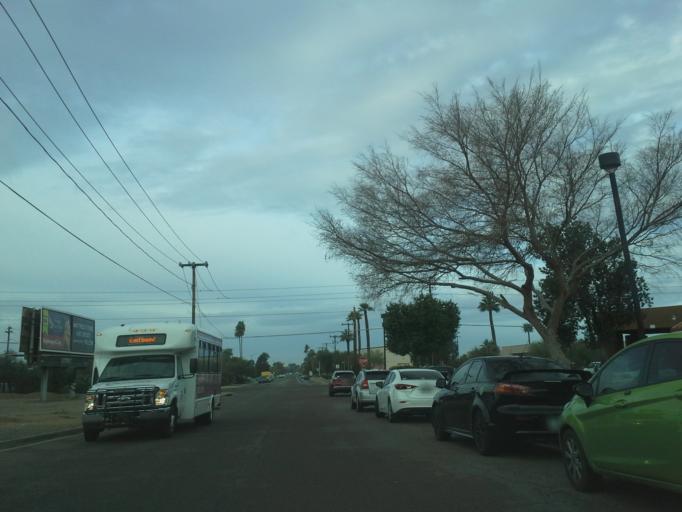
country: US
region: Arizona
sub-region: Maricopa County
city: Glendale
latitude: 33.5894
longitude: -112.0986
